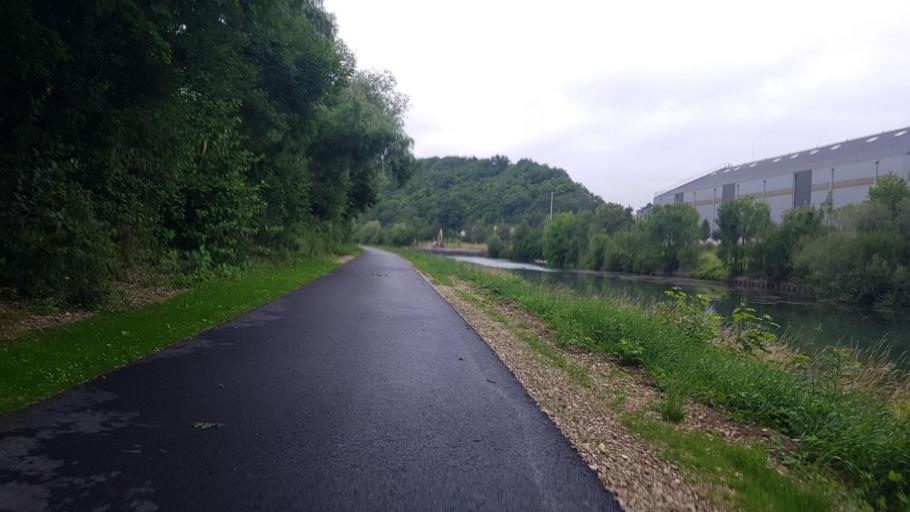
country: FR
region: Champagne-Ardenne
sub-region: Departement de la Marne
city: Vitry-le-Francois
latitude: 48.7663
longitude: 4.5593
